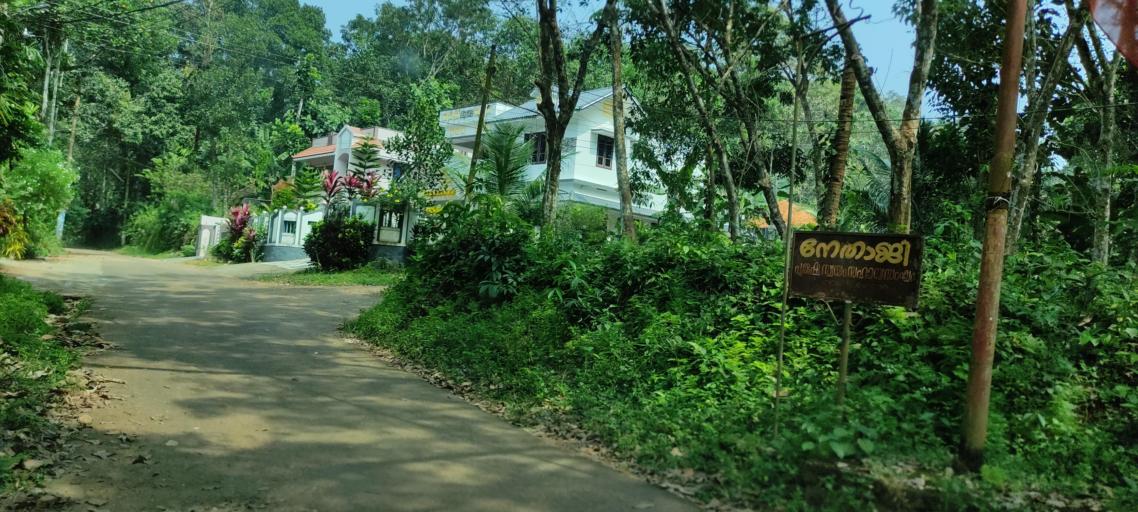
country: IN
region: Kerala
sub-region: Pattanamtitta
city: Adur
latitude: 9.2102
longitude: 76.6944
